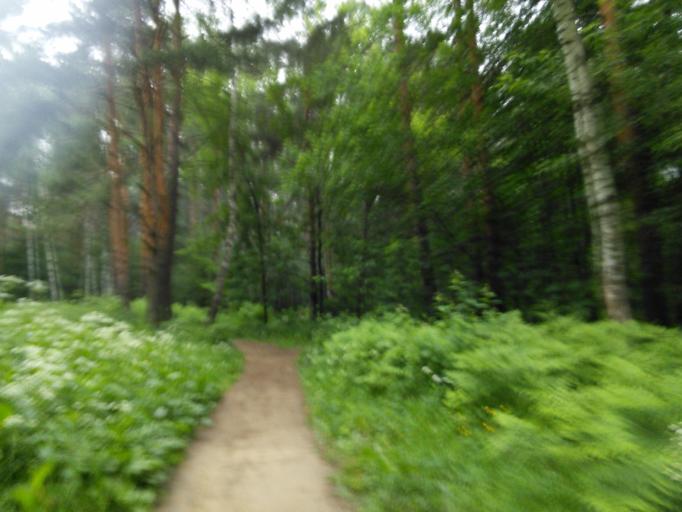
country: RU
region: Moskovskaya
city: Dzerzhinskiy
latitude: 55.6444
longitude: 37.8687
